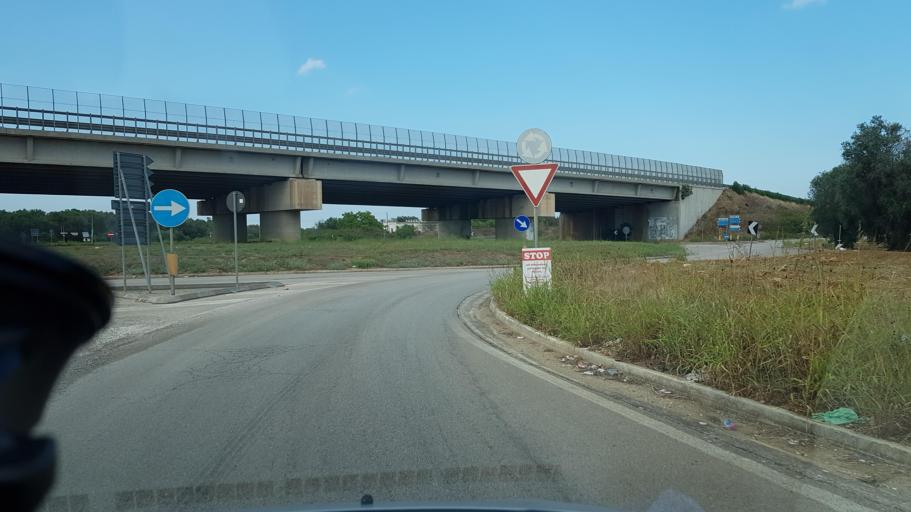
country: IT
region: Apulia
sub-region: Provincia di Brindisi
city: Latiano
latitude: 40.5476
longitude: 17.7039
